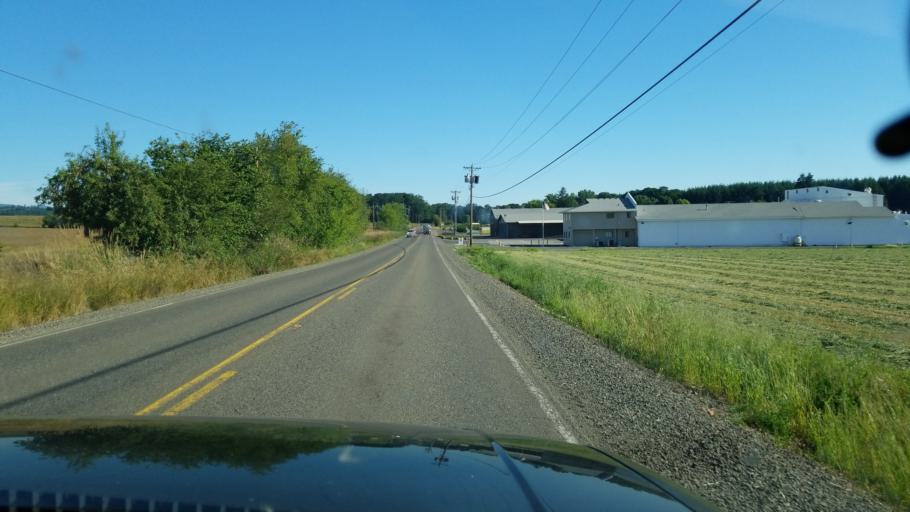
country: US
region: Oregon
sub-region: Yamhill County
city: Carlton
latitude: 45.2910
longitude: -123.2041
